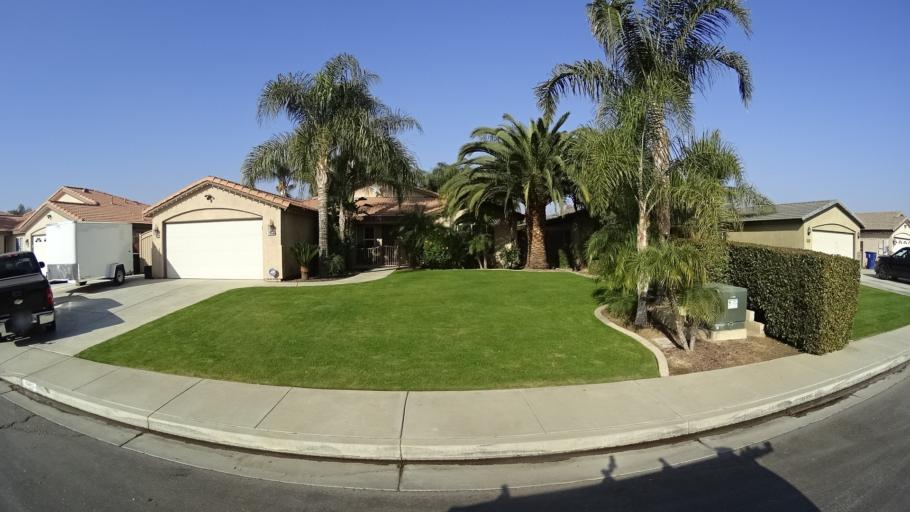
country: US
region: California
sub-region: Kern County
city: Greenacres
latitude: 35.3943
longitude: -119.0684
